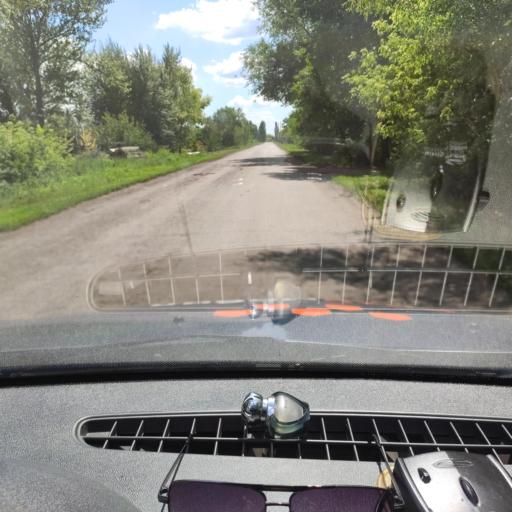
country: RU
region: Voronezj
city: Maslovka
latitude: 51.5133
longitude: 39.2972
